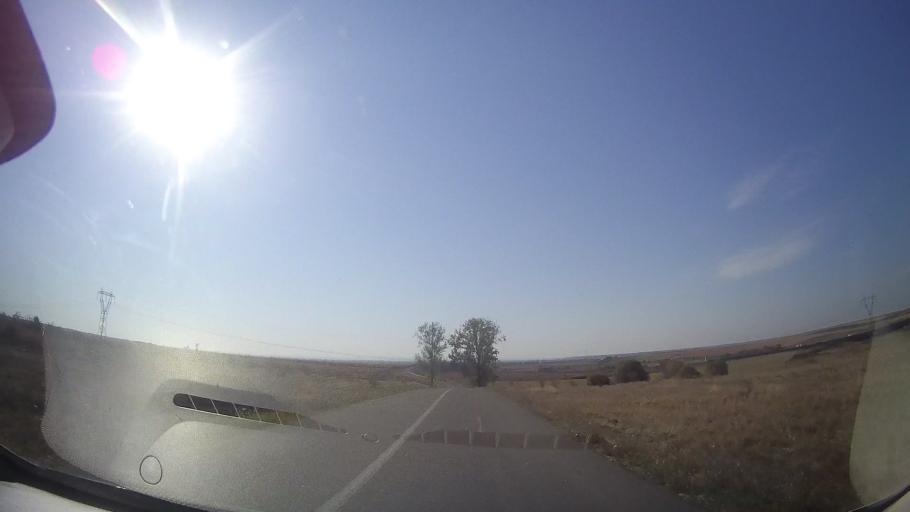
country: RO
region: Timis
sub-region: Comuna Topolovatu Mare
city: Topolovatu Mare
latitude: 45.8098
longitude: 21.5837
